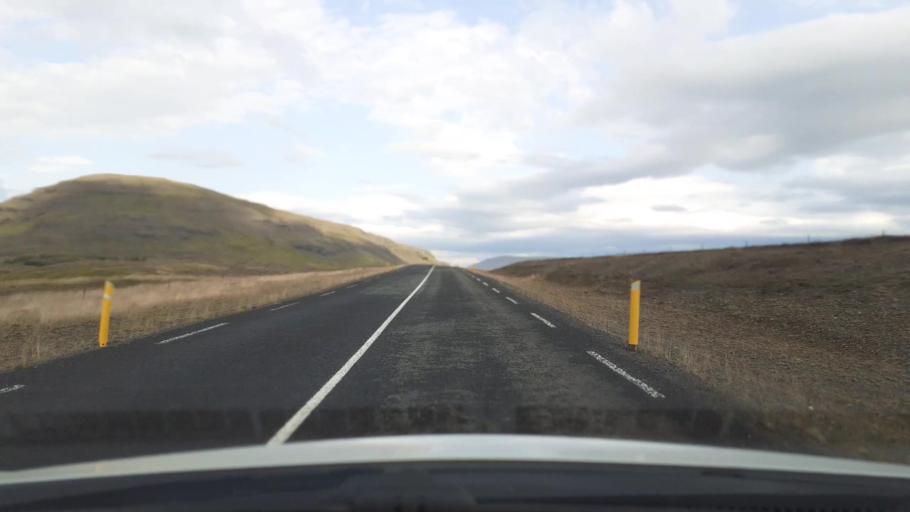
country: IS
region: Capital Region
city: Mosfellsbaer
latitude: 64.3046
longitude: -21.4925
